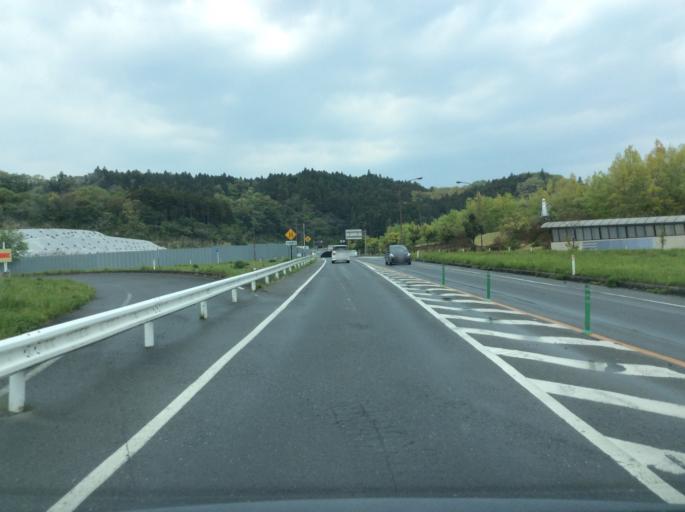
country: JP
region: Fukushima
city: Iwaki
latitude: 37.0261
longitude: 140.8828
